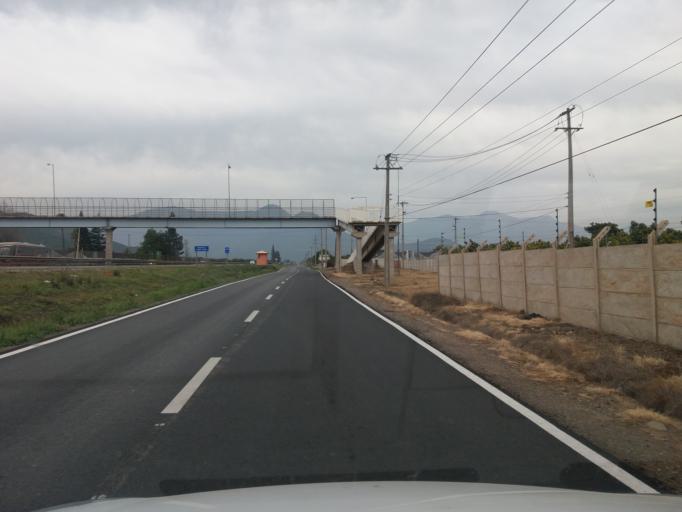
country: CL
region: Valparaiso
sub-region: Provincia de Quillota
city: Hacienda La Calera
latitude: -32.8298
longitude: -71.1283
